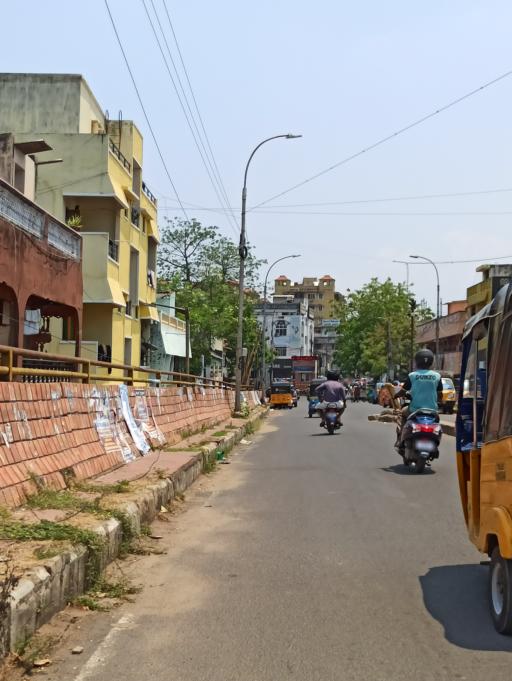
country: IN
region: Tamil Nadu
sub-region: Chennai
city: Chetput
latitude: 13.0677
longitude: 80.2317
